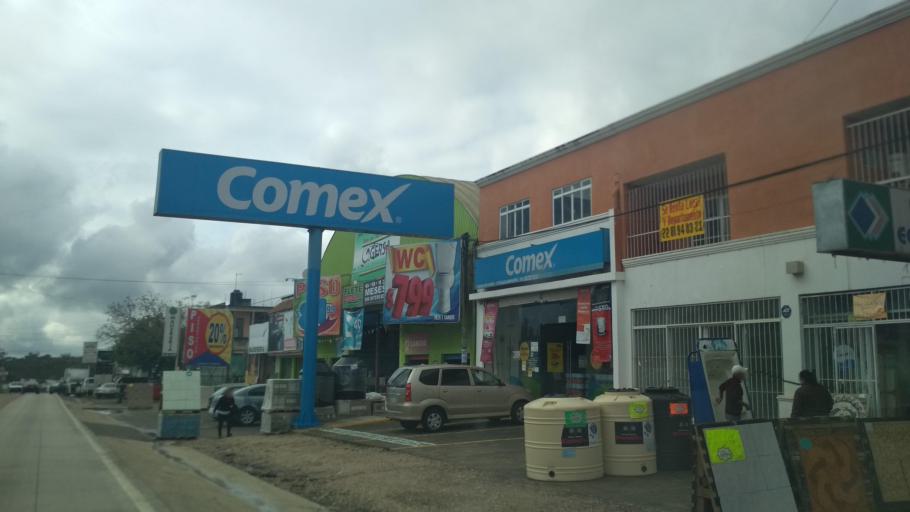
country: MX
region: Veracruz
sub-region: Emiliano Zapata
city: Las Trancas
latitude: 19.4980
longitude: -96.8603
